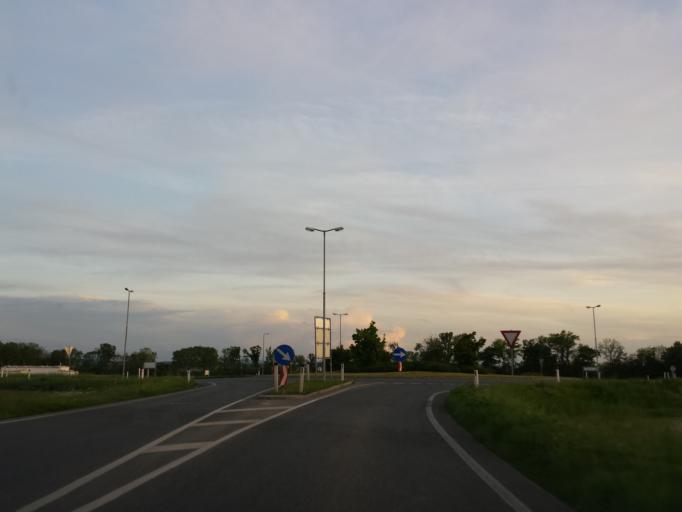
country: AT
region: Lower Austria
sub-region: Politischer Bezirk Tulln
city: Michelhausen
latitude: 48.3288
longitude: 15.9555
